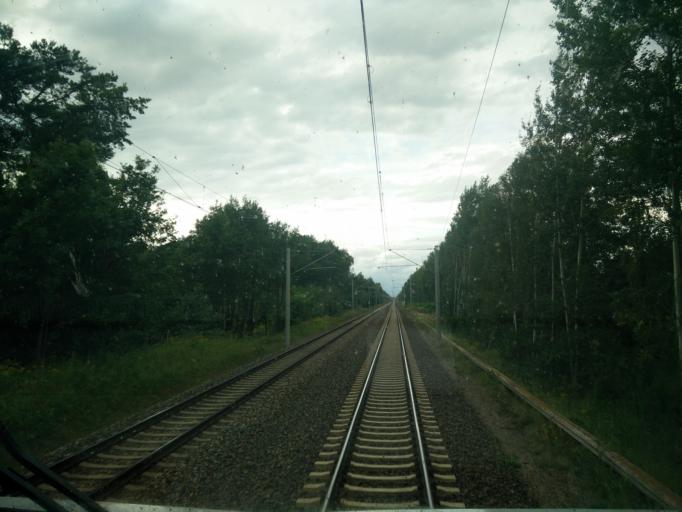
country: DE
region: Brandenburg
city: Kasel-Golzig
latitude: 51.9934
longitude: 13.7740
